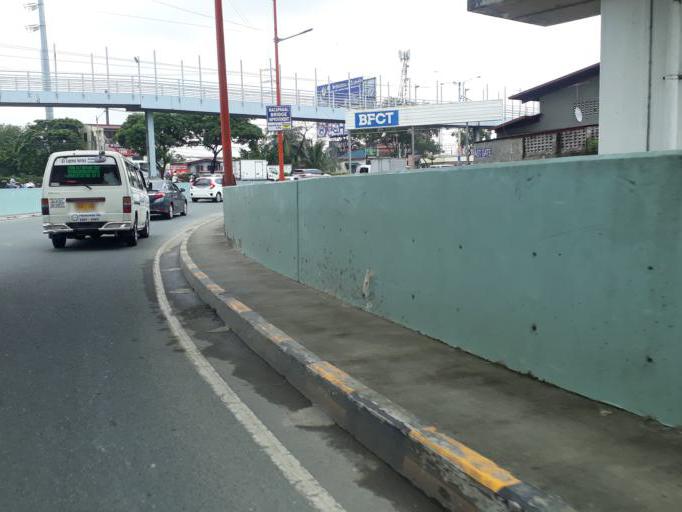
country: PH
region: Metro Manila
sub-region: Marikina
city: Calumpang
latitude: 14.6241
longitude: 121.0838
